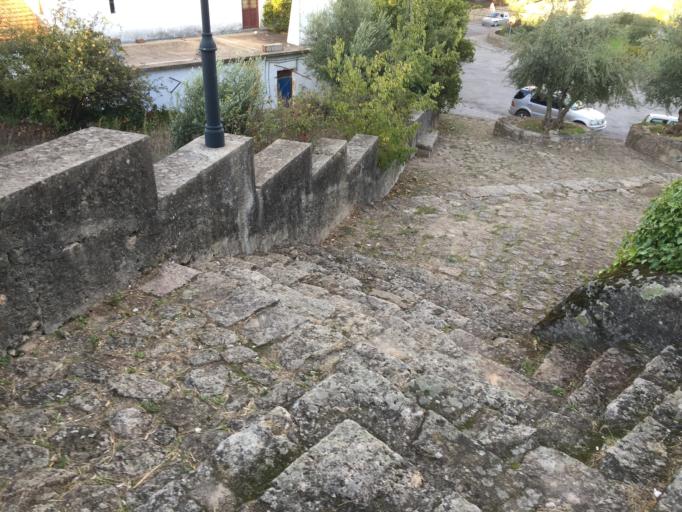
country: PT
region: Portalegre
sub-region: Alter do Chao
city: Alter do Chao
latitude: 39.2874
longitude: -7.6432
